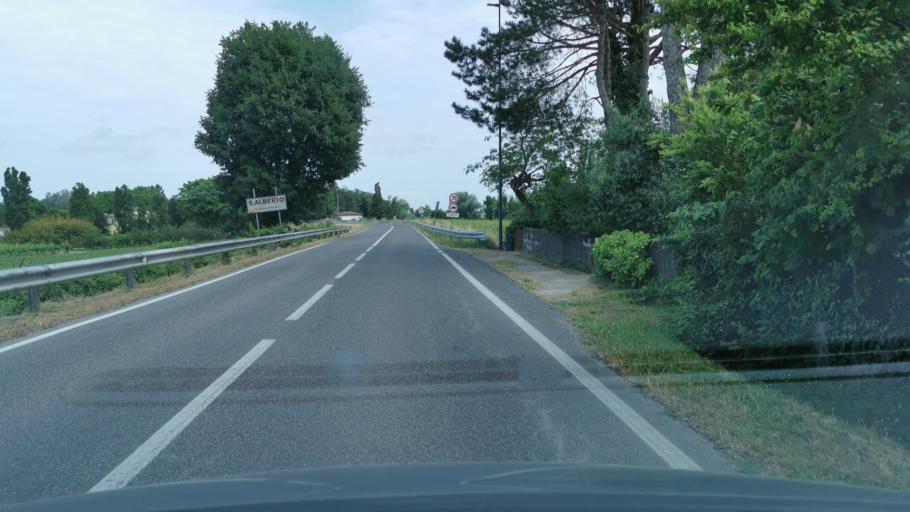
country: IT
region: Emilia-Romagna
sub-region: Provincia di Ravenna
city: Sant'Alberto
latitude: 44.5357
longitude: 12.1719
